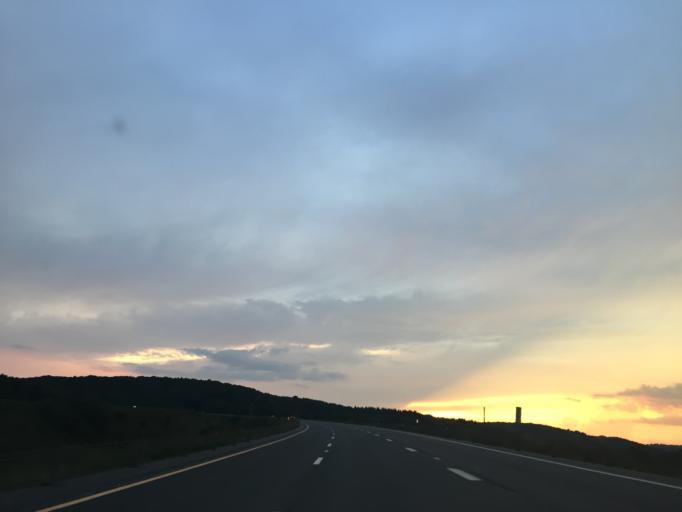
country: US
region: New York
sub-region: Chenango County
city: Greene
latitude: 42.1976
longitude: -75.6660
